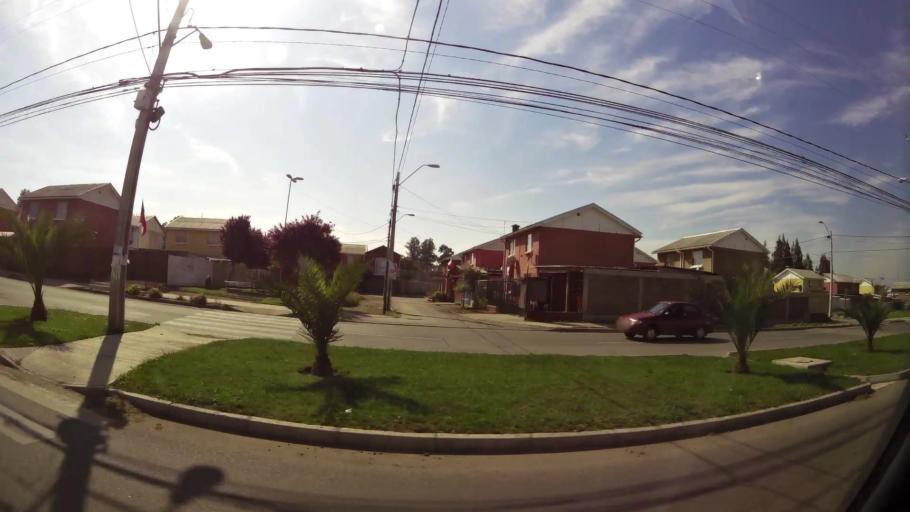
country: CL
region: Santiago Metropolitan
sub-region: Provincia de Talagante
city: El Monte
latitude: -33.6821
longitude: -70.9546
